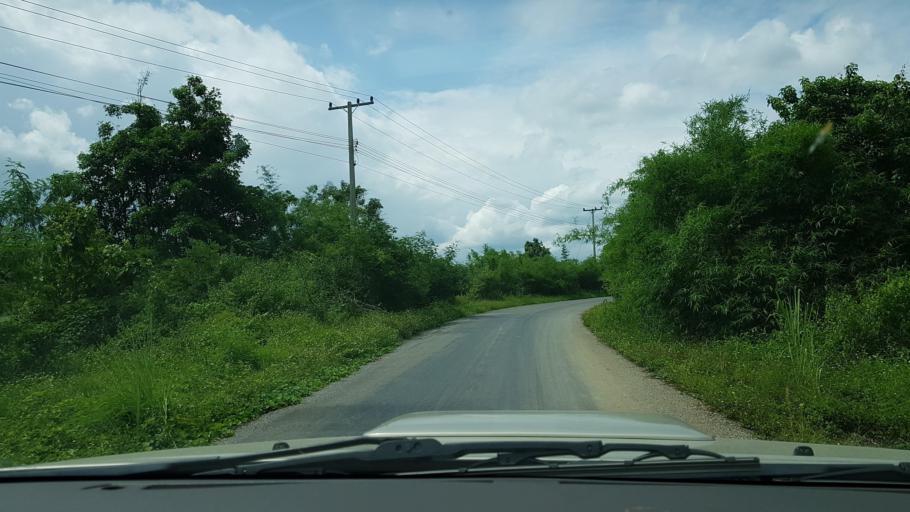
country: LA
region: Loungnamtha
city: Muang Nale
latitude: 20.2423
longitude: 101.5766
